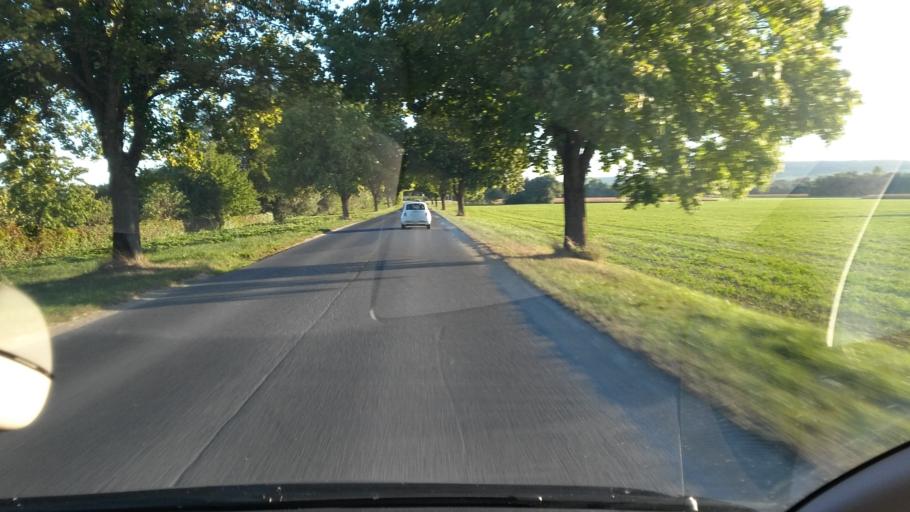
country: FR
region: Champagne-Ardenne
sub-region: Departement de la Marne
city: Mareuil-sur-Ay
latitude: 49.0408
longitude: 4.0405
